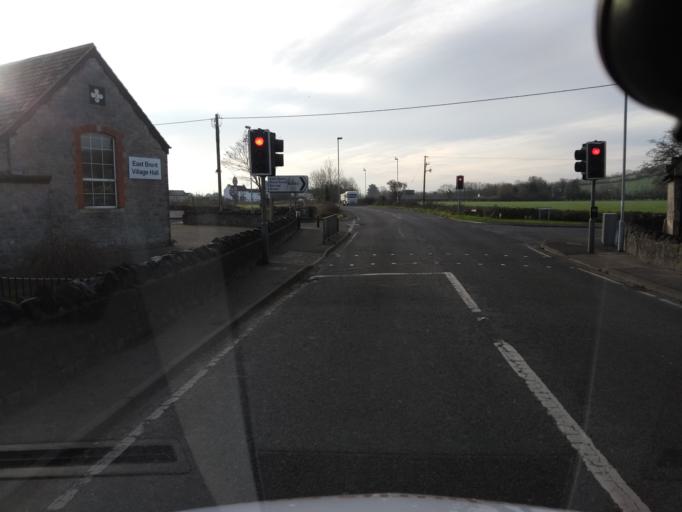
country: GB
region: England
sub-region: North Somerset
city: Bleadon
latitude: 51.2635
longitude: -2.9348
